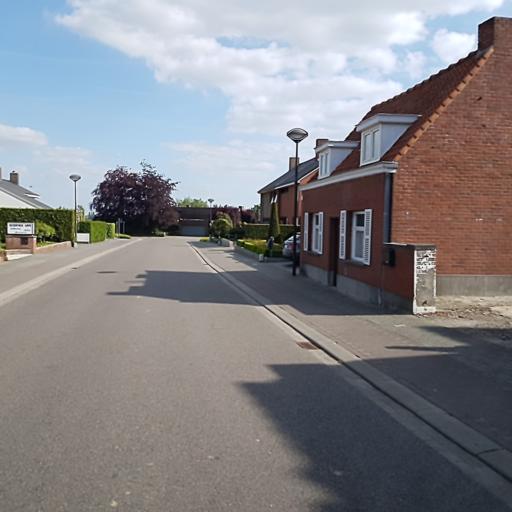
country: BE
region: Flanders
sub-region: Provincie West-Vlaanderen
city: Tielt
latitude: 50.9932
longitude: 3.3347
